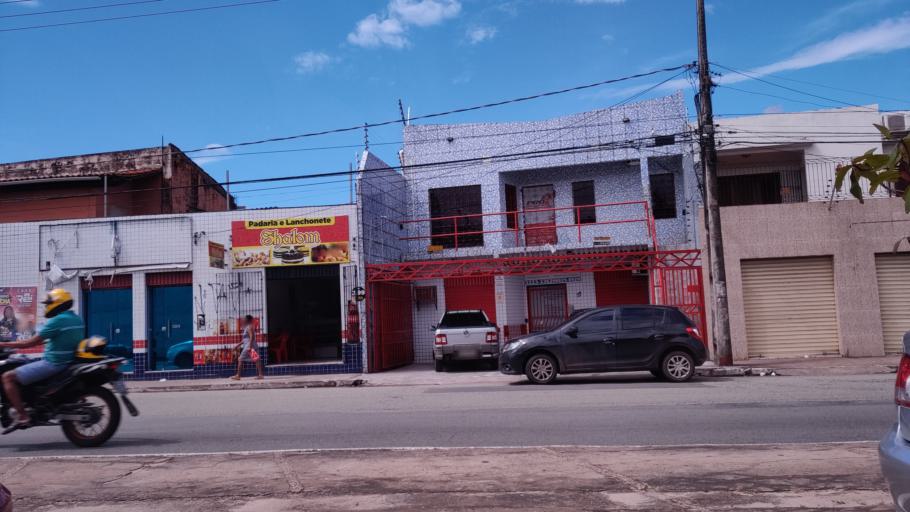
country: BR
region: Maranhao
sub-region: Sao Luis
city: Sao Luis
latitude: -2.5383
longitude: -44.2690
